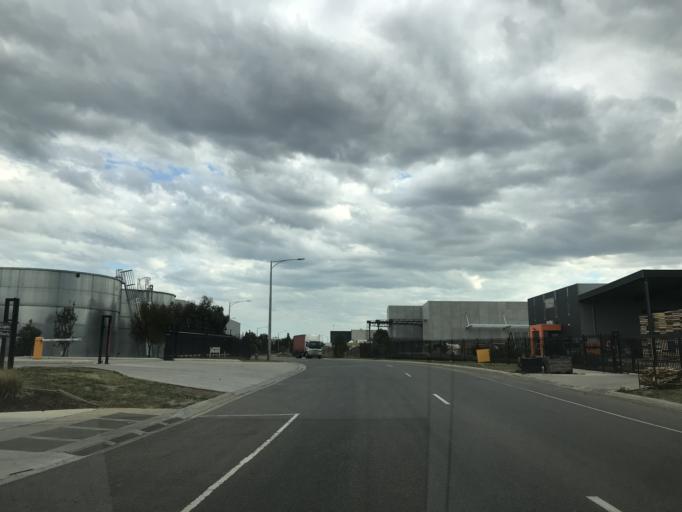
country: AU
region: Victoria
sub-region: Wyndham
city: Truganina
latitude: -37.8153
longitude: 144.7387
